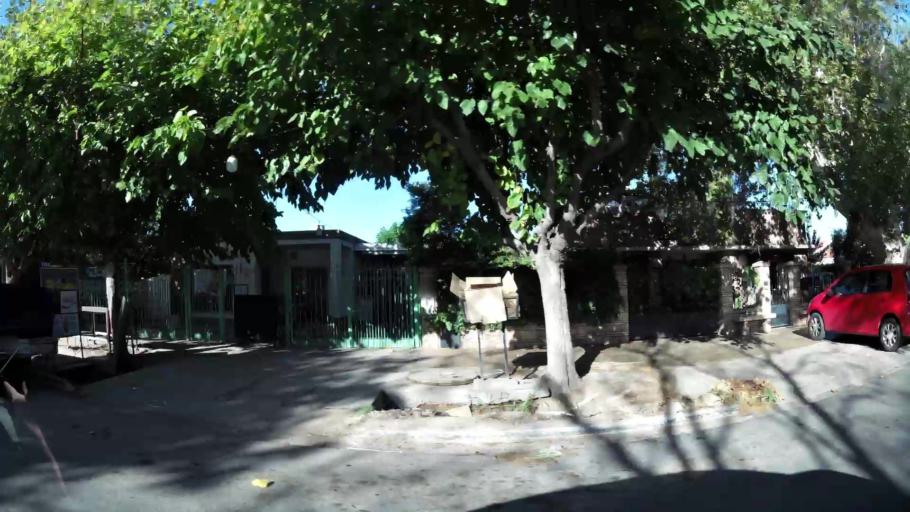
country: AR
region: San Juan
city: Villa Krause
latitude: -31.5702
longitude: -68.5194
